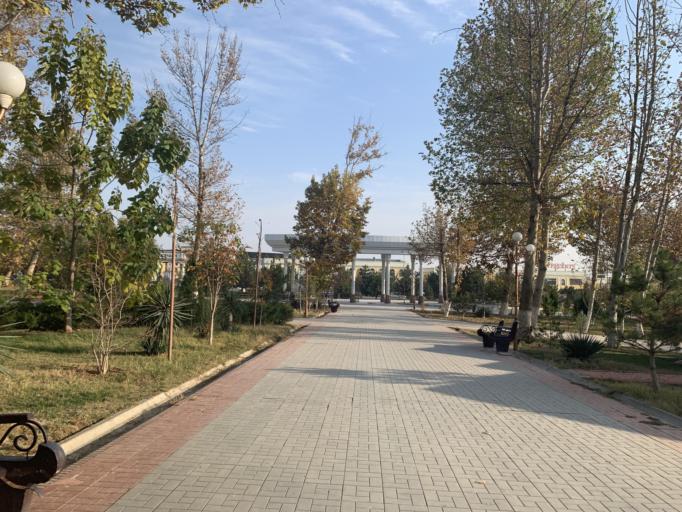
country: UZ
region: Namangan
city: Namangan Shahri
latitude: 40.9989
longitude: 71.5967
